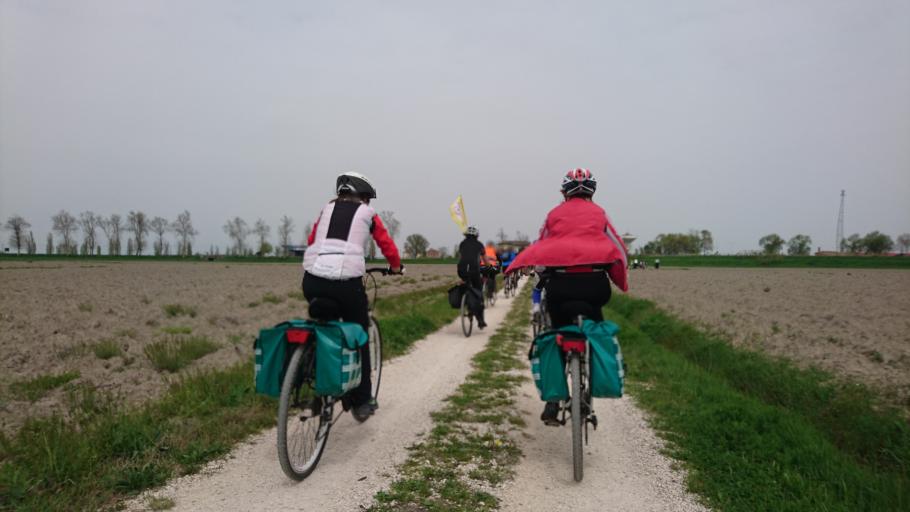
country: IT
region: Veneto
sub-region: Provincia di Venezia
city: Concordia Sagittaria
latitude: 45.7019
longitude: 12.8669
